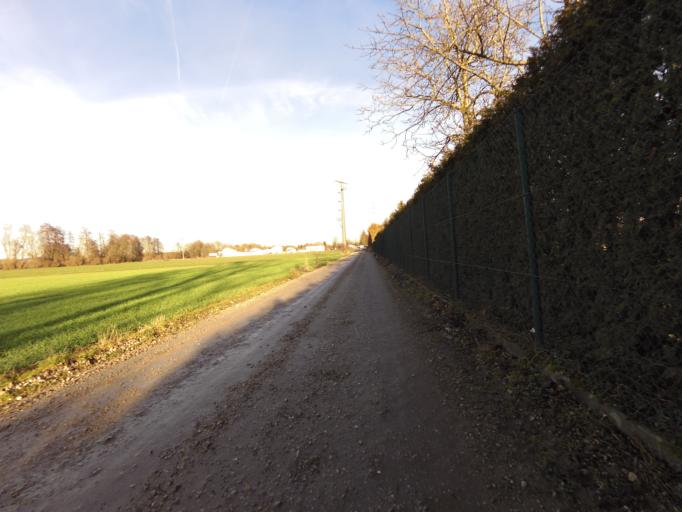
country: DE
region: Bavaria
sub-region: Lower Bavaria
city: Bruckberg
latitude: 48.4889
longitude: 12.0190
